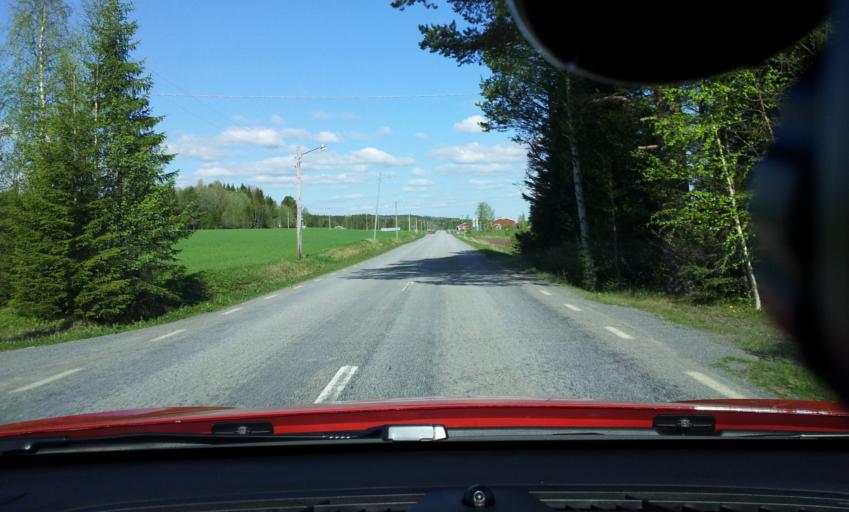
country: SE
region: Jaemtland
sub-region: Krokoms Kommun
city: Krokom
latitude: 63.1616
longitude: 14.1287
